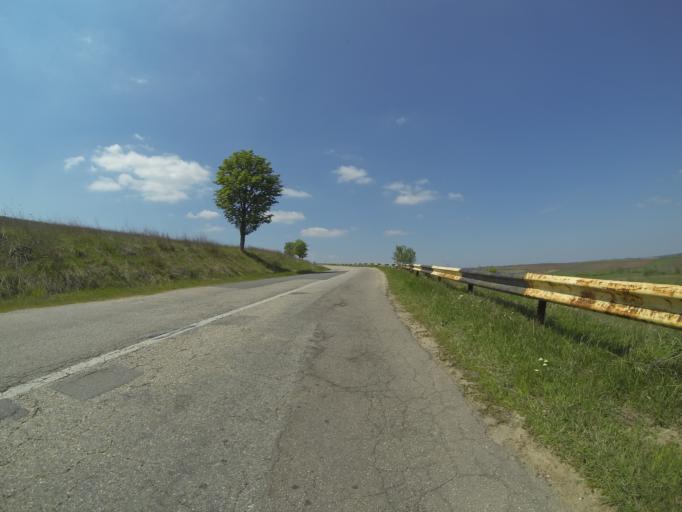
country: RO
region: Dolj
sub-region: Comuna Salcuta
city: Salcuta
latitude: 44.2567
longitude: 23.4455
